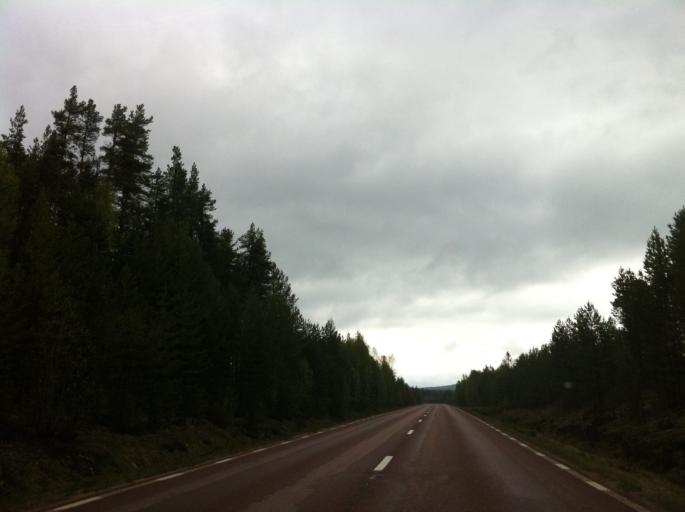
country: SE
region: Jaemtland
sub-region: Harjedalens Kommun
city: Sveg
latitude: 61.9743
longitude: 14.5781
